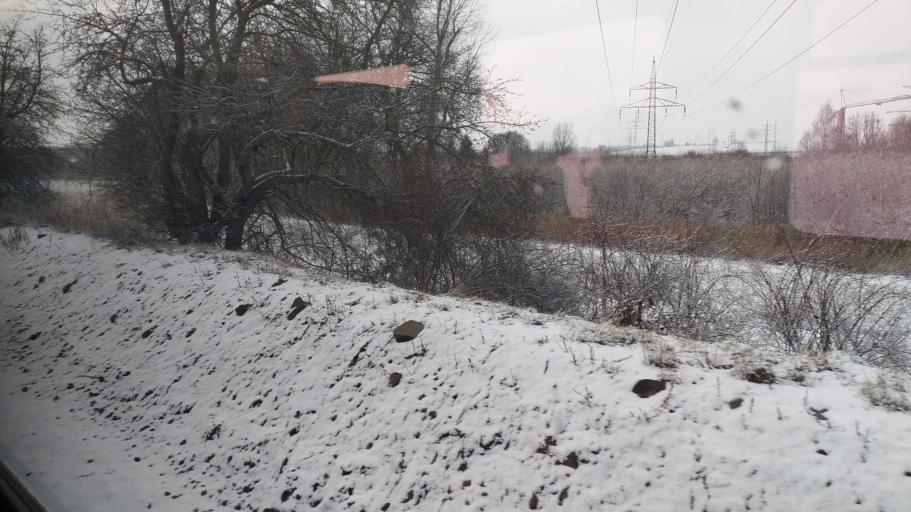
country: CZ
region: Central Bohemia
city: Trebotov
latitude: 50.0293
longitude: 14.2947
